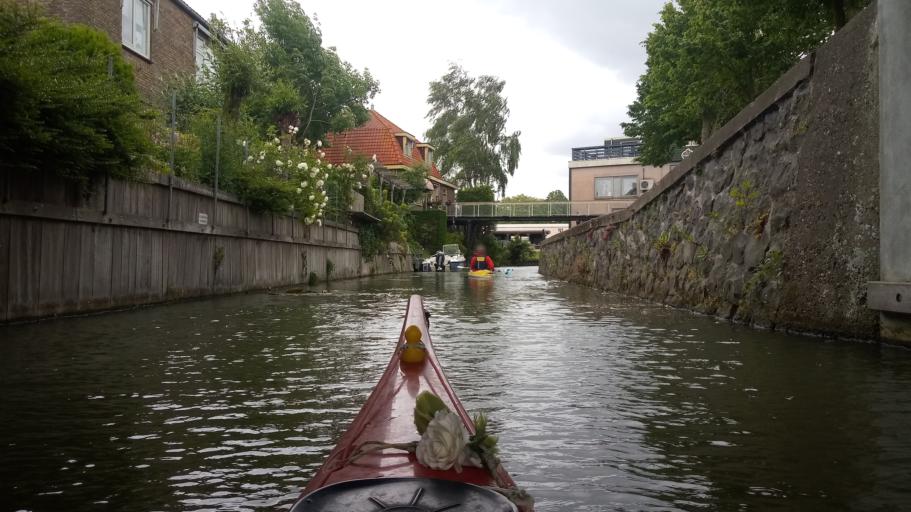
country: NL
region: North Holland
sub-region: Gemeente Enkhuizen
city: Enkhuizen
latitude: 52.6885
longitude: 5.2530
